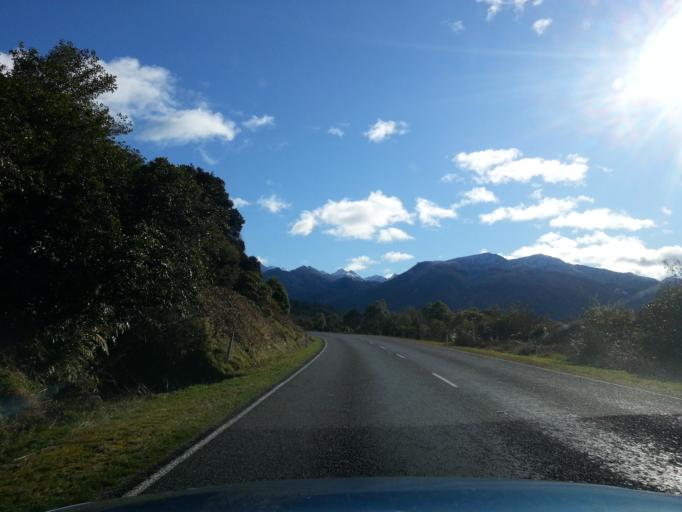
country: NZ
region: West Coast
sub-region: Grey District
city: Greymouth
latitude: -42.7422
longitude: 171.4709
